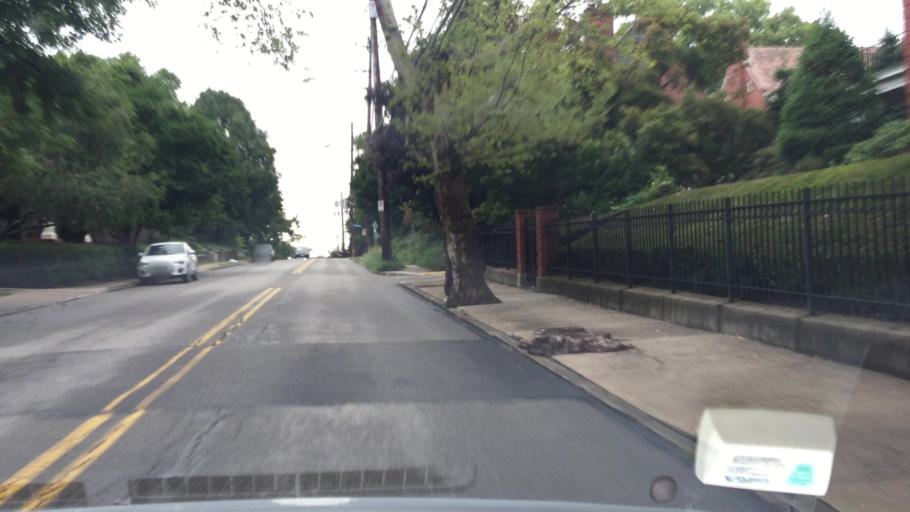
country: US
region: Pennsylvania
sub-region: Allegheny County
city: Bloomfield
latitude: 40.4466
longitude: -79.9275
